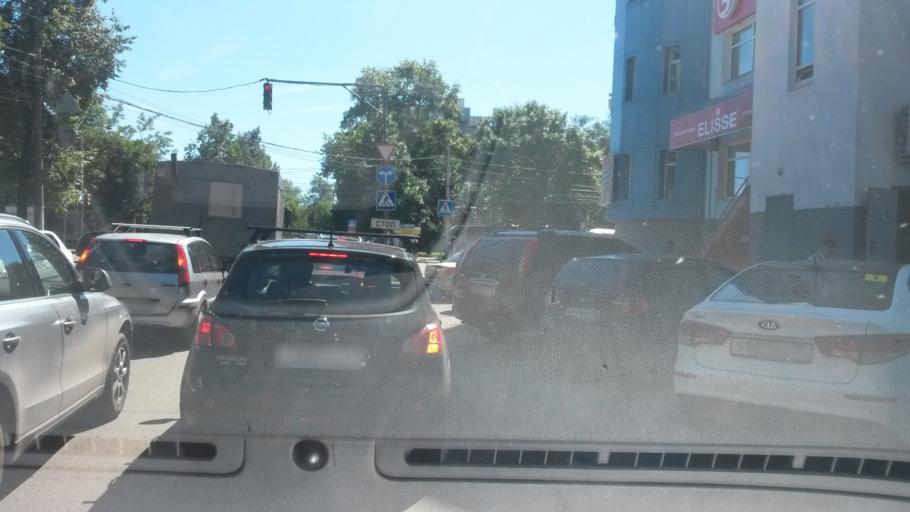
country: RU
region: Jaroslavl
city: Yaroslavl
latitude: 57.6306
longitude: 39.8687
